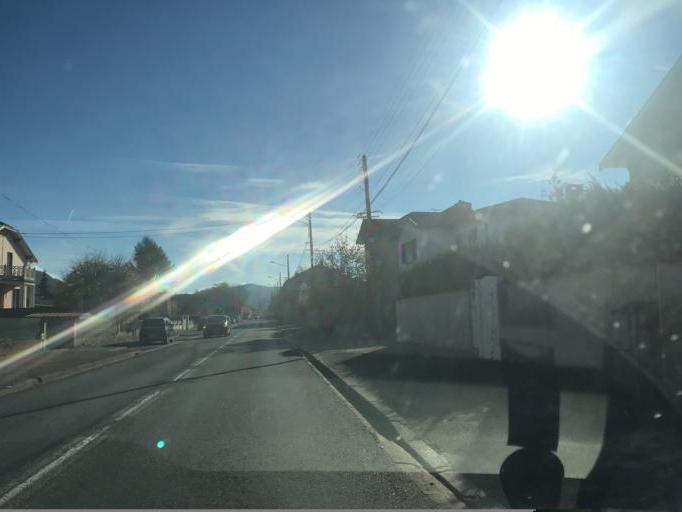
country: FR
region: Rhone-Alpes
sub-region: Departement de l'Ain
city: Amberieu-en-Bugey
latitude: 45.9701
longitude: 5.3531
